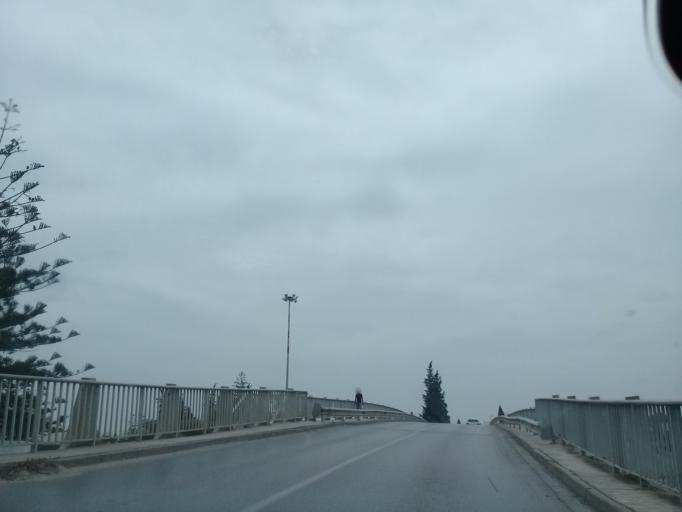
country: TN
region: Tunis
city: Tunis
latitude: 36.8387
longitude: 10.1646
